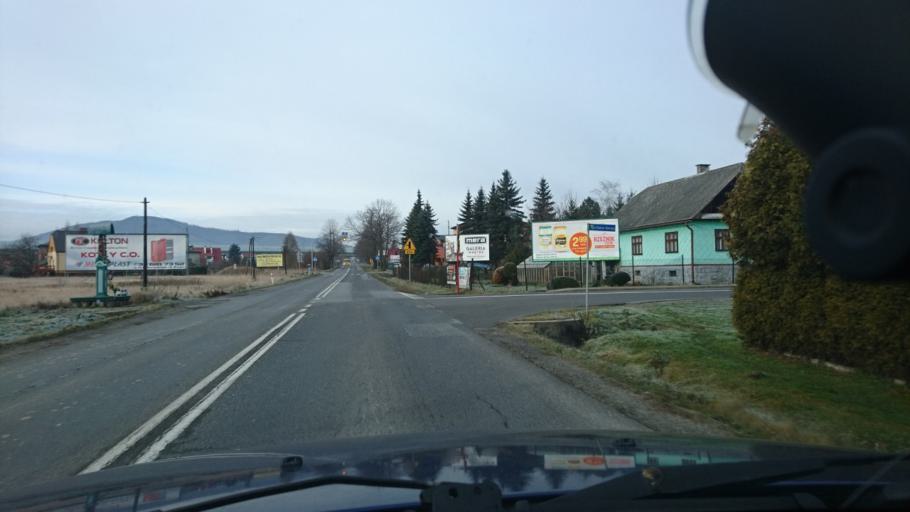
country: PL
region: Silesian Voivodeship
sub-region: Powiat zywiecki
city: Lodygowice
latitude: 49.7318
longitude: 19.1230
